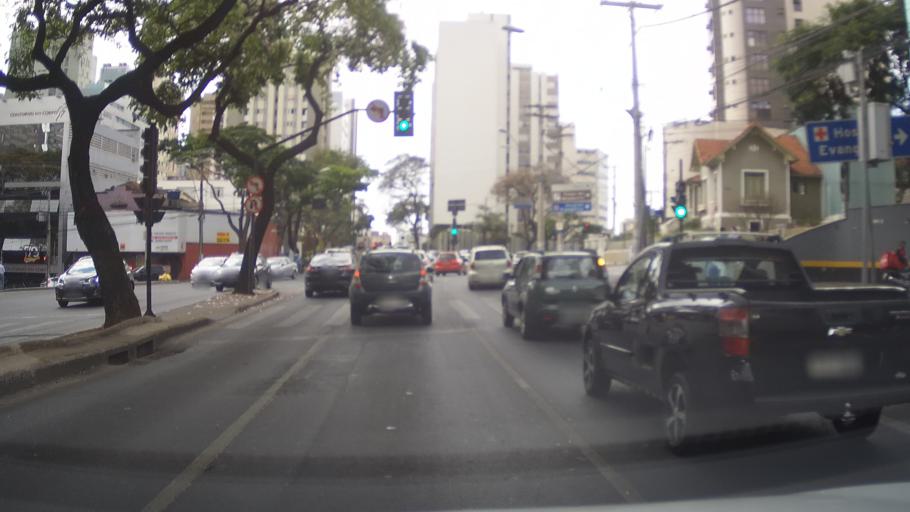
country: BR
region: Minas Gerais
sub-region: Belo Horizonte
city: Belo Horizonte
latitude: -19.9324
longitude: -43.9242
